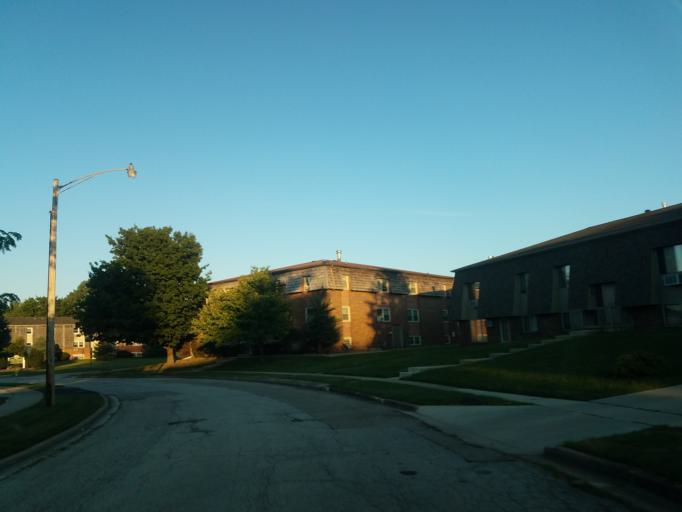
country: US
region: Illinois
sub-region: McLean County
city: Bloomington
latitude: 40.4692
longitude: -88.9508
